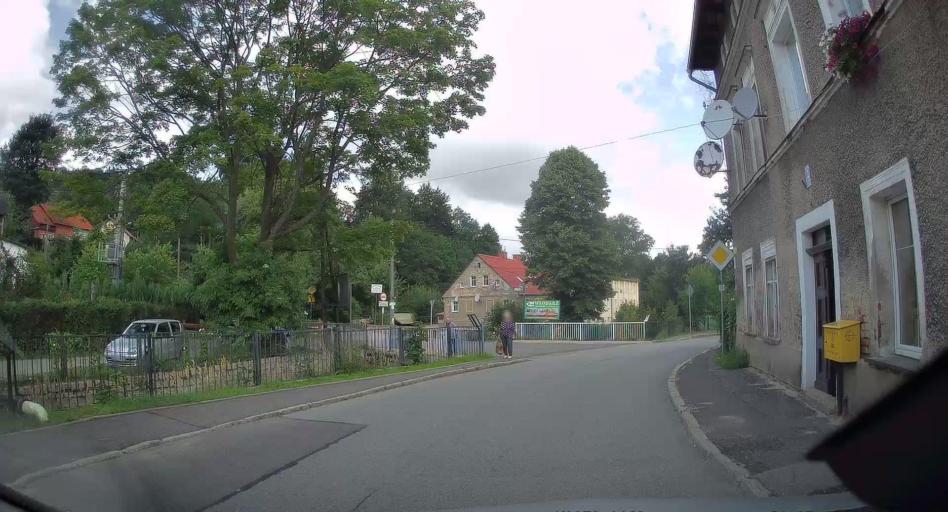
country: PL
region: Lower Silesian Voivodeship
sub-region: Powiat walbrzyski
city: Walim
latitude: 50.6976
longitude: 16.4418
